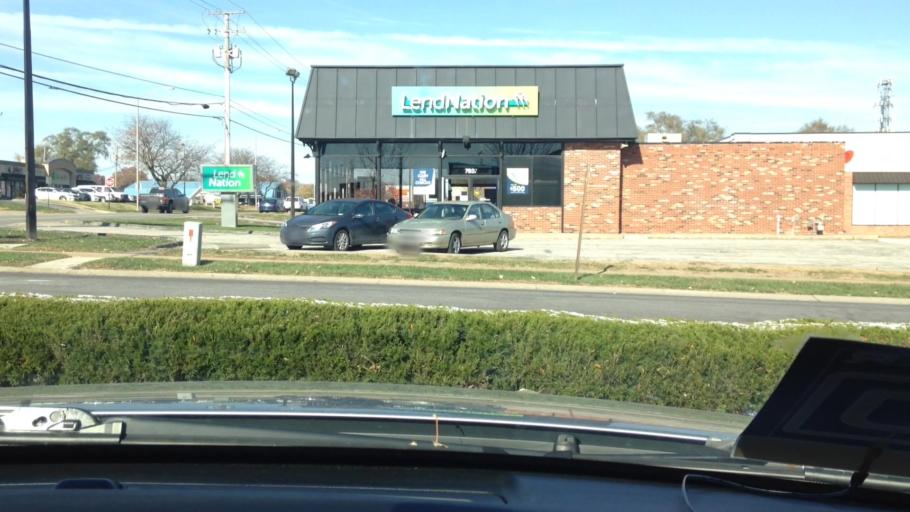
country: US
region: Kansas
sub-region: Johnson County
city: Overland Park
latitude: 38.9898
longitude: -94.6677
